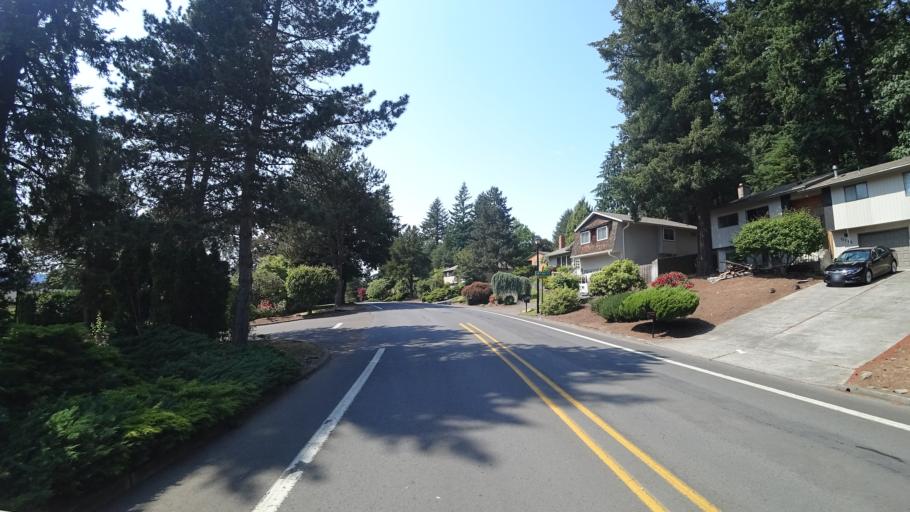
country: US
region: Oregon
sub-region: Clackamas County
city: Happy Valley
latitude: 45.4451
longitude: -122.5644
